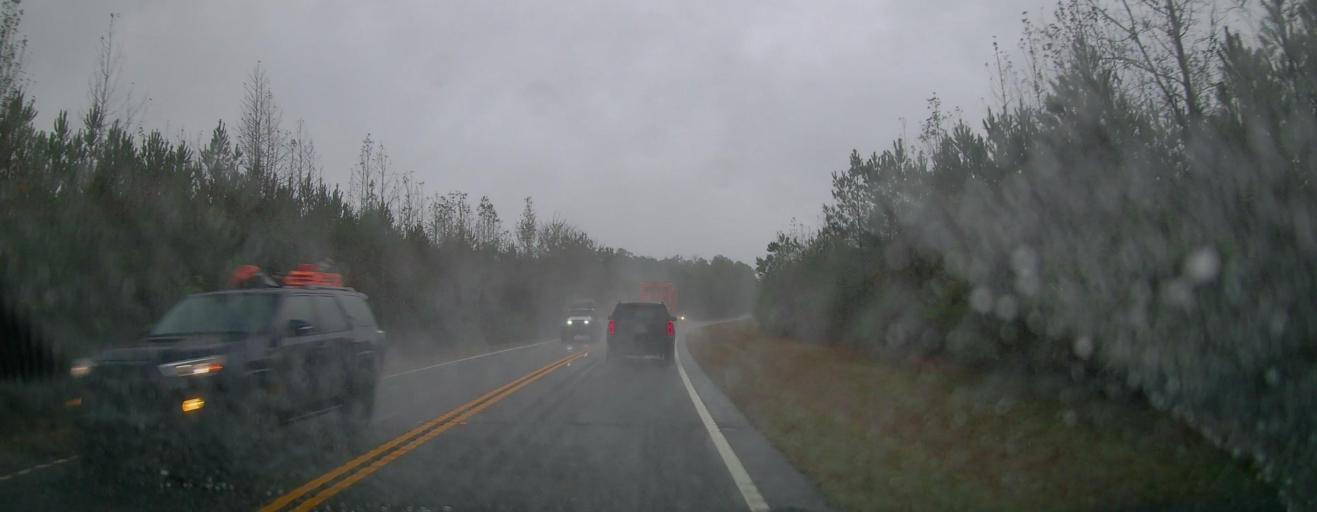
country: US
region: Georgia
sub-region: Jones County
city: Gray
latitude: 33.1003
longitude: -83.4866
